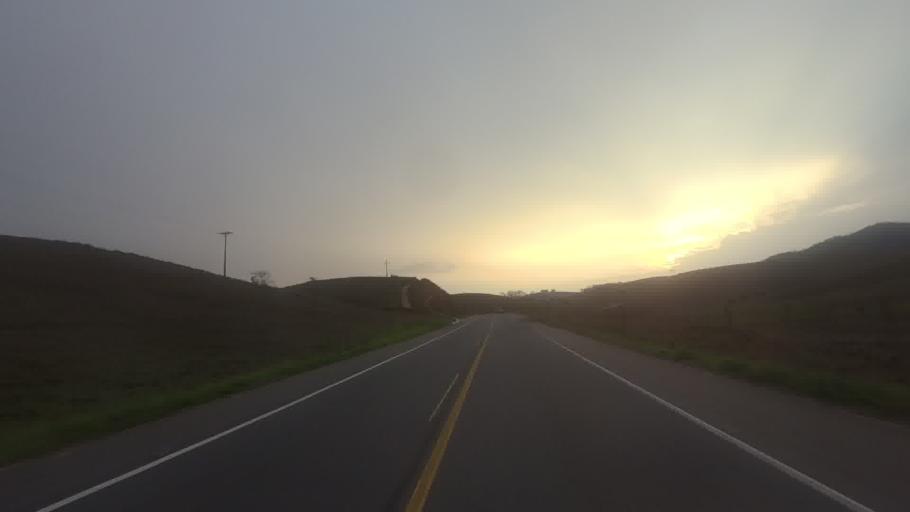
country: BR
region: Rio de Janeiro
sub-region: Carmo
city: Carmo
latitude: -21.7583
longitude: -42.4872
